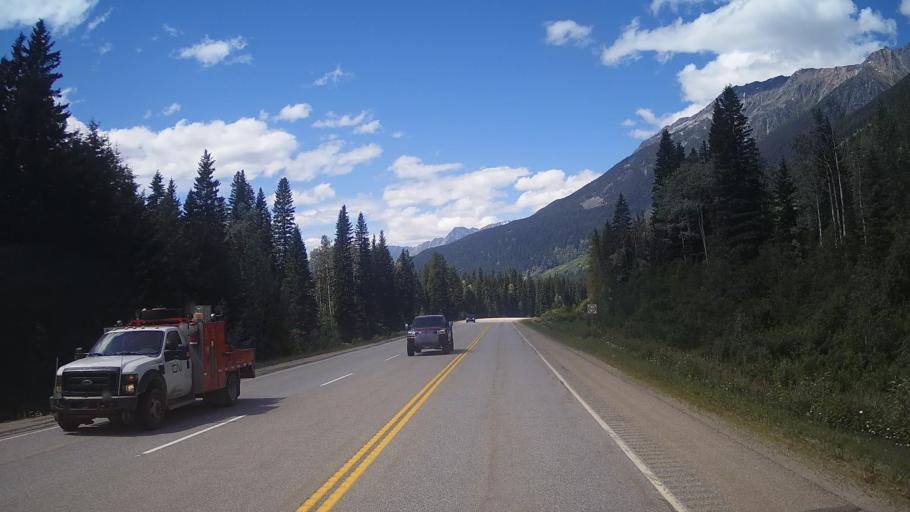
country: CA
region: Alberta
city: Grande Cache
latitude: 53.0084
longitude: -119.0604
